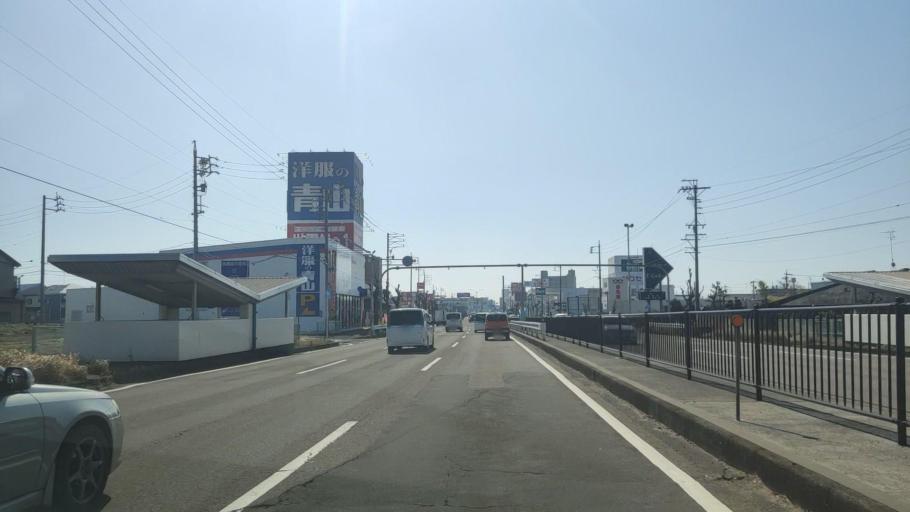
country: JP
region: Gifu
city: Gifu-shi
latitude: 35.3988
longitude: 136.7849
